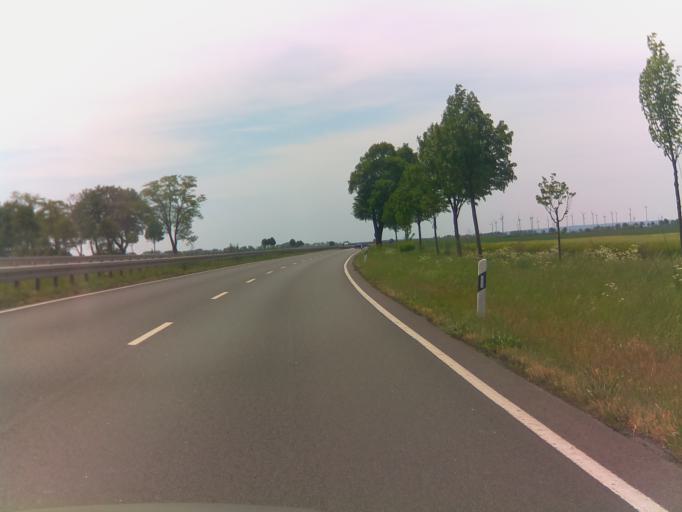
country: DE
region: Saxony-Anhalt
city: Hohendodeleben
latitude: 52.0260
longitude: 11.5164
